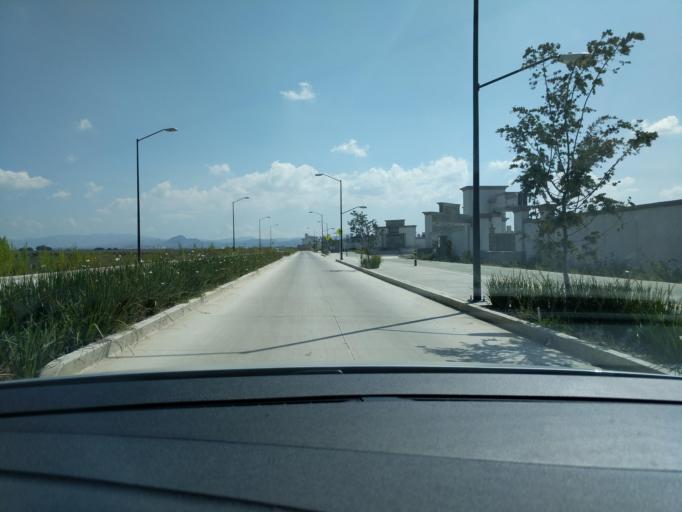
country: MX
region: Hidalgo
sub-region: Zempoala
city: Jagueey de Tellez (Estacion Tellez)
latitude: 20.0066
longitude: -98.7759
